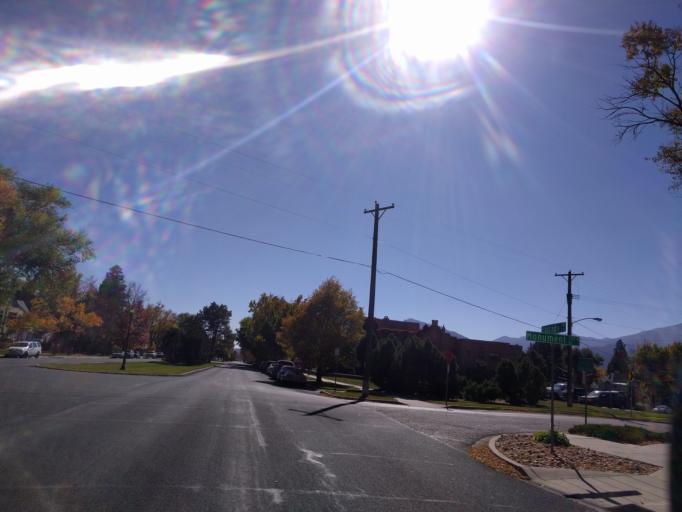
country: US
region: Colorado
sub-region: El Paso County
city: Colorado Springs
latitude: 38.8441
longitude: -104.8249
